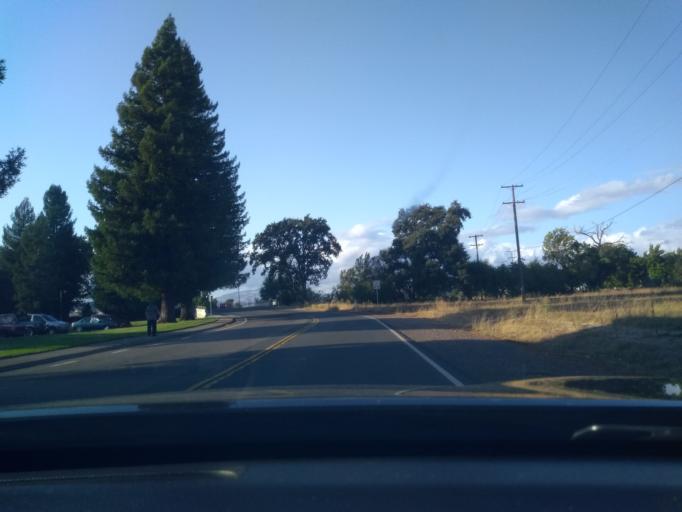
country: US
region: California
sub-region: Mendocino County
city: Ukiah
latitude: 39.1573
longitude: -123.1993
